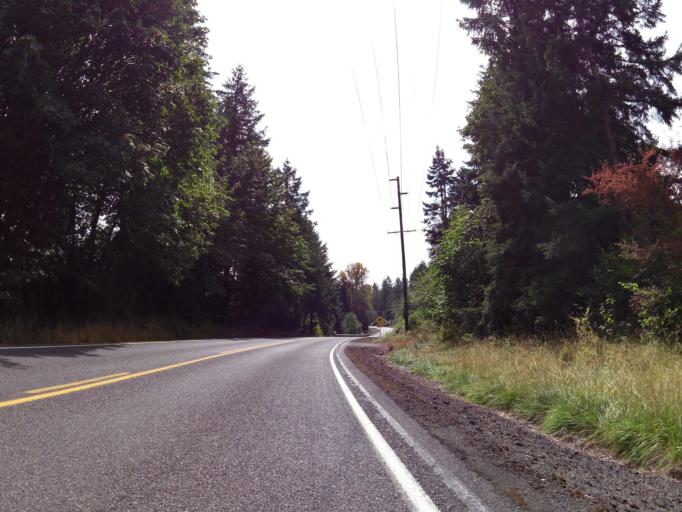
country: US
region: Washington
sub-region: Lewis County
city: Winlock
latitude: 46.4335
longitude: -122.9702
